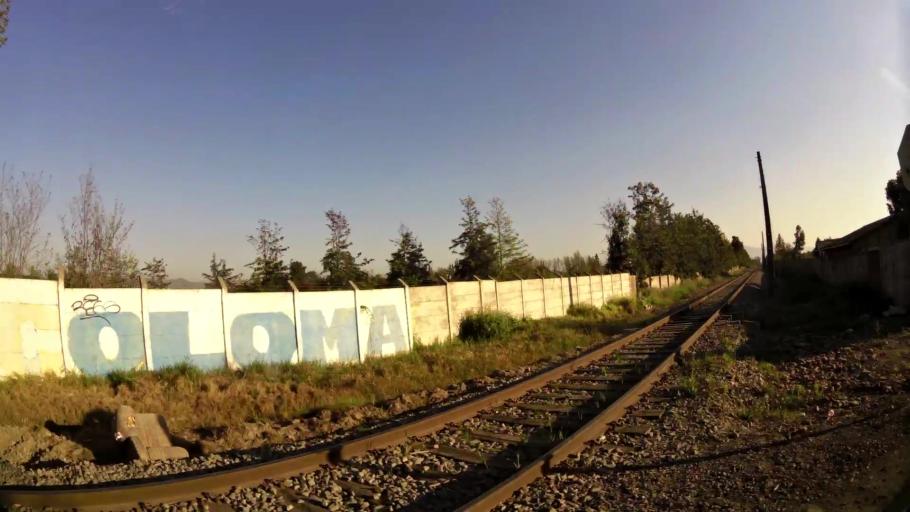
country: CL
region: Santiago Metropolitan
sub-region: Provincia de Talagante
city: Penaflor
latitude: -33.6204
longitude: -70.8691
